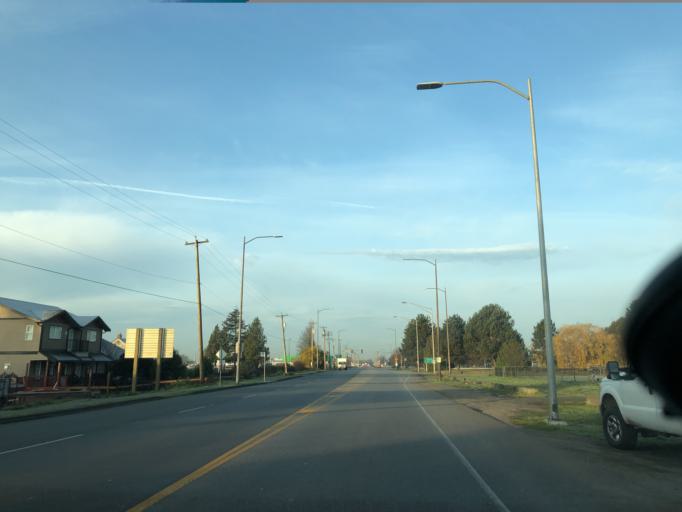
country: CA
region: British Columbia
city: Richmond
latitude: 49.1922
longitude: -123.1471
